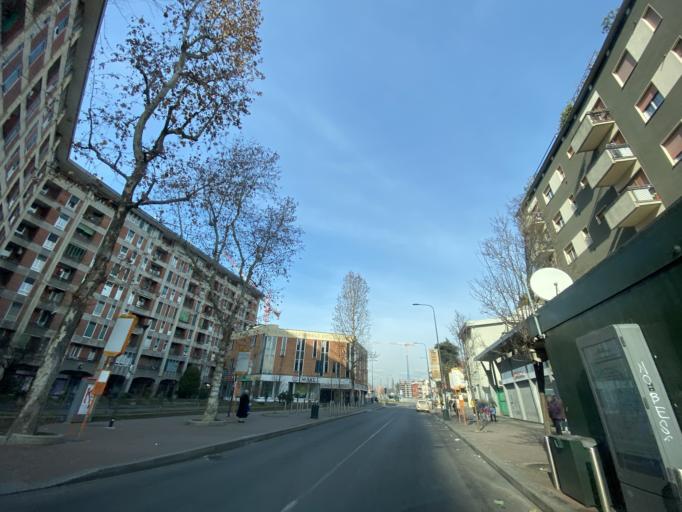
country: IT
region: Lombardy
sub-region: Citta metropolitana di Milano
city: Cormano
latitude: 45.5200
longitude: 9.1698
